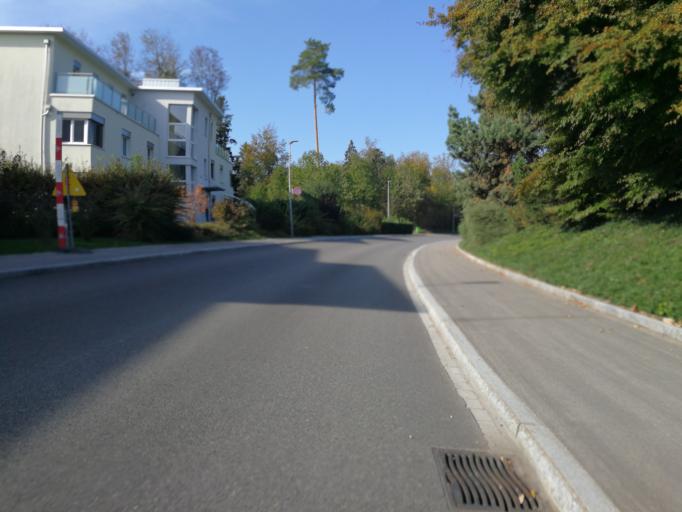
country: CH
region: Zurich
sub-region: Bezirk Hinwil
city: Hadlikon
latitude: 47.2764
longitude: 8.8716
